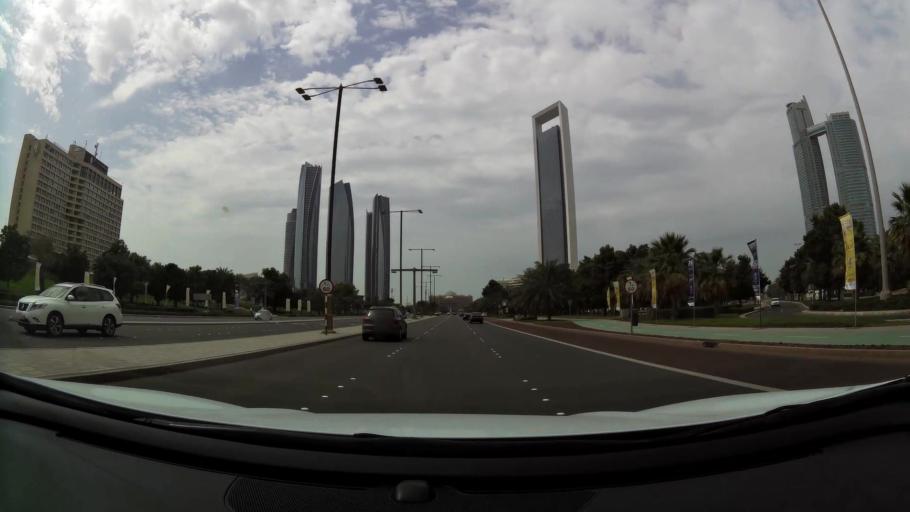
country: AE
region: Abu Dhabi
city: Abu Dhabi
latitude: 24.4590
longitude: 54.3303
